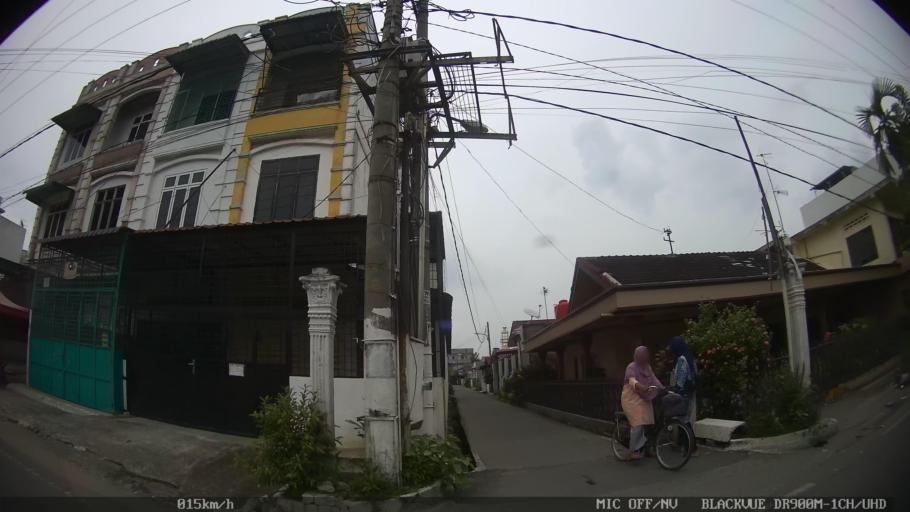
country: ID
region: North Sumatra
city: Medan
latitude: 3.5801
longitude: 98.7020
